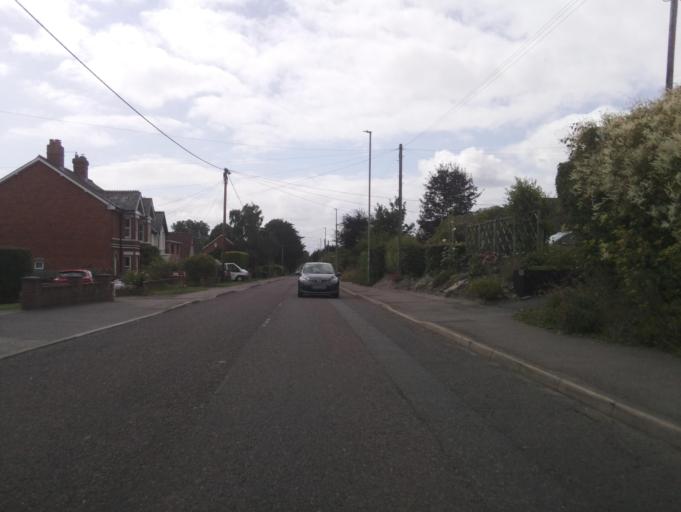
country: GB
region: England
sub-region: Dorset
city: Blandford Forum
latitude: 50.8673
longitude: -2.1515
